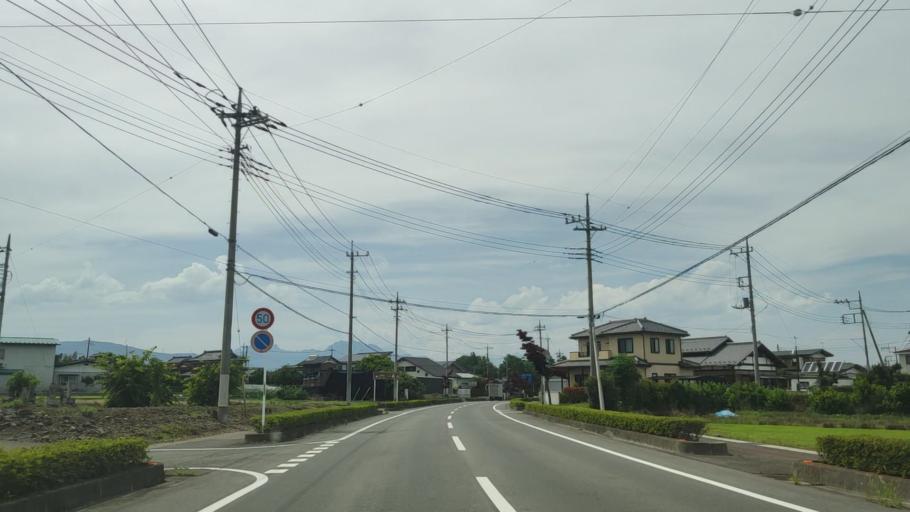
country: JP
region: Gunma
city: Tomioka
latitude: 36.2486
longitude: 138.8842
